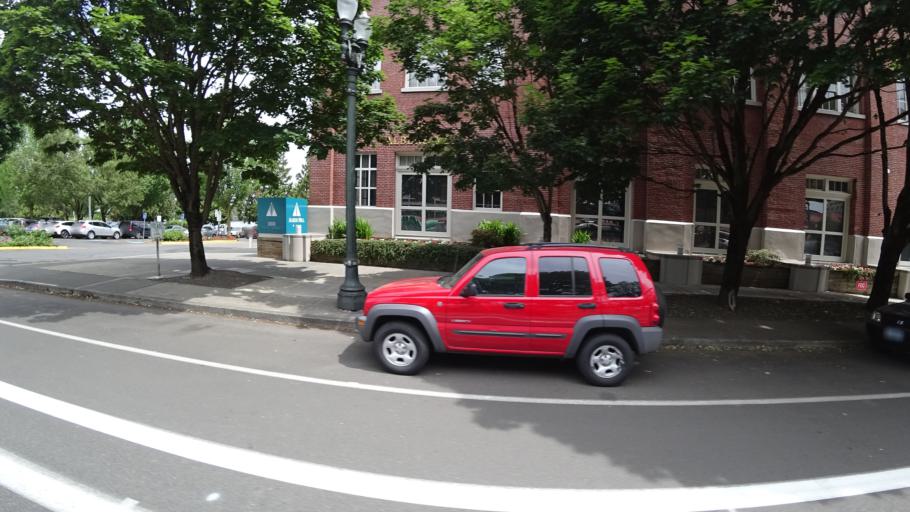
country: US
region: Oregon
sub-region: Multnomah County
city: Portland
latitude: 45.5310
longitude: -122.6766
